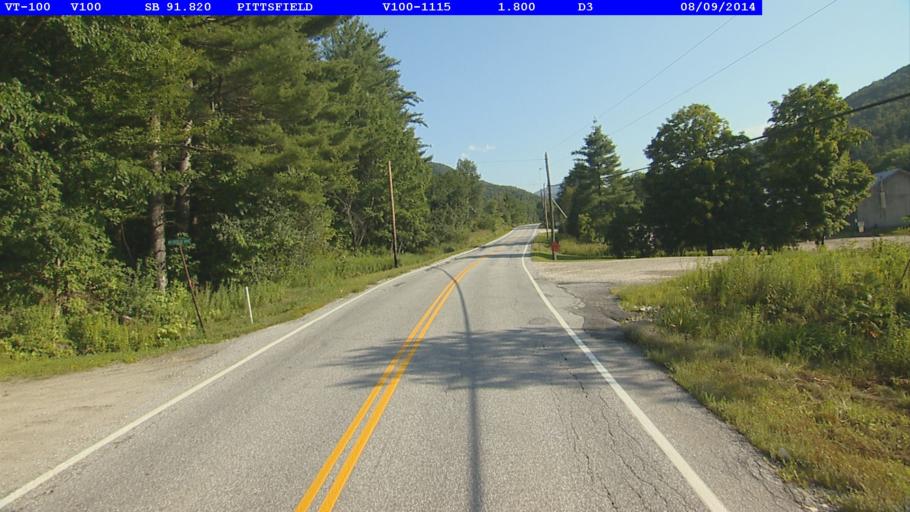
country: US
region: Vermont
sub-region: Rutland County
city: Rutland
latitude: 43.7430
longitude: -72.8200
